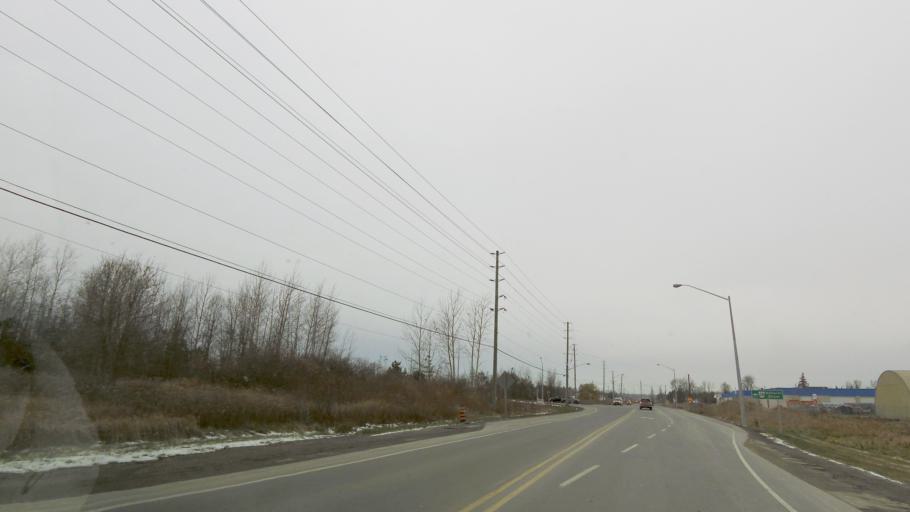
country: CA
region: Ontario
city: Newmarket
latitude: 44.1055
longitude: -79.5166
